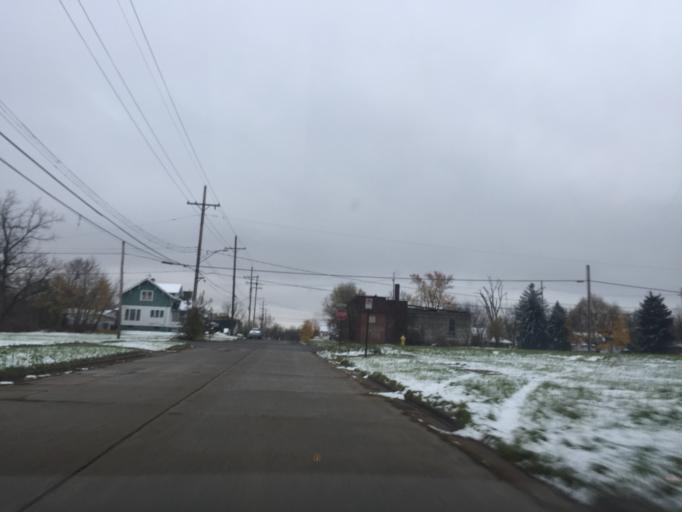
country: US
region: Michigan
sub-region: Oakland County
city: Pontiac
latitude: 42.6268
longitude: -83.2791
